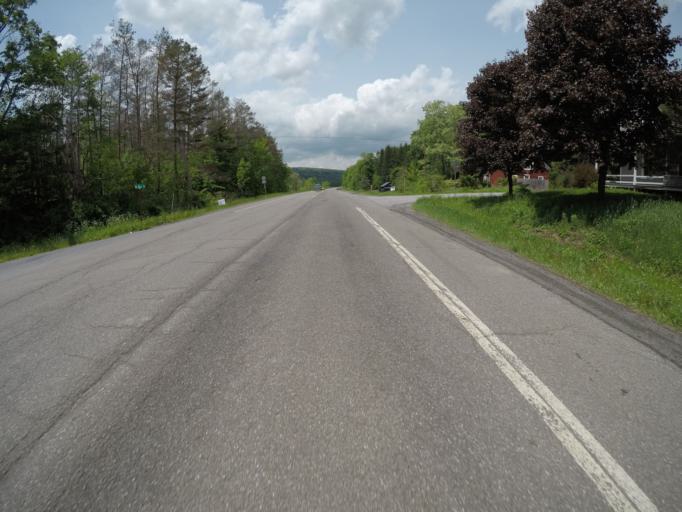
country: US
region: New York
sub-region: Delaware County
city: Stamford
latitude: 42.2280
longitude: -74.5942
